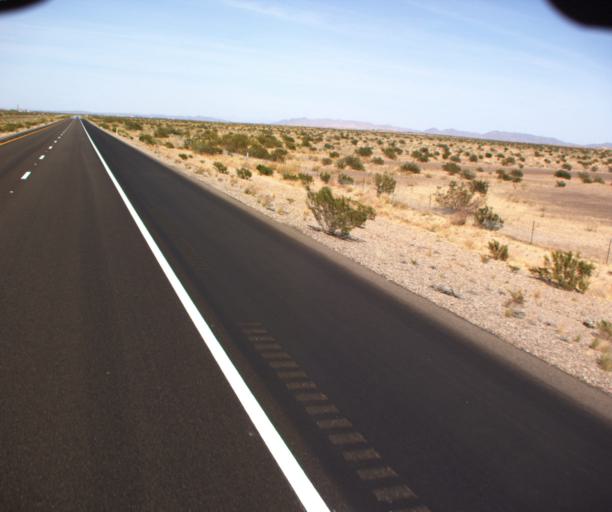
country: US
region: Arizona
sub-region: Yuma County
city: Somerton
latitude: 32.5705
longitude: -114.5568
